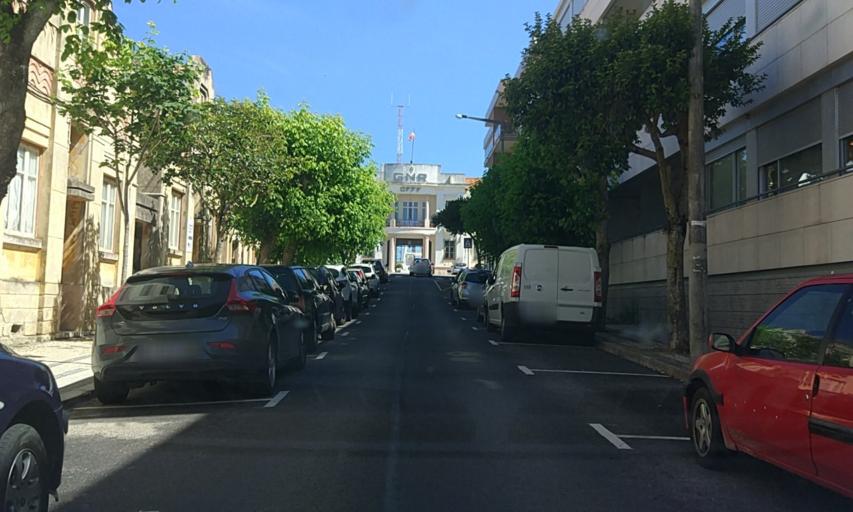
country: PT
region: Coimbra
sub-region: Figueira da Foz
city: Figueira da Foz
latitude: 40.1517
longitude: -8.8502
